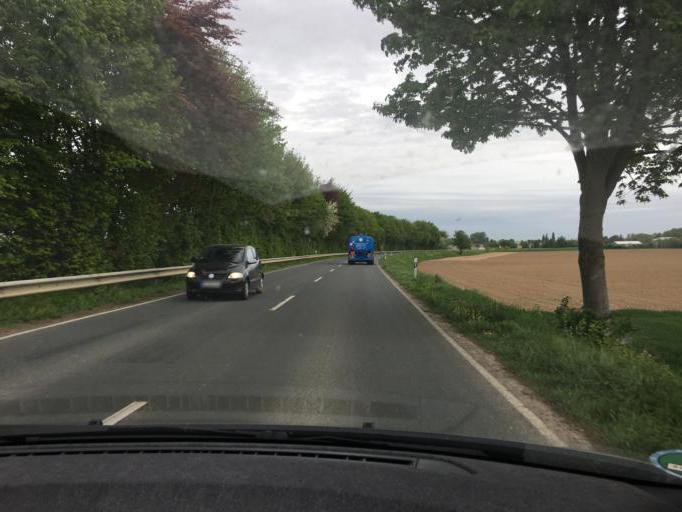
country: DE
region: North Rhine-Westphalia
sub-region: Regierungsbezirk Koln
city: Titz
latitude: 51.0433
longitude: 6.4300
